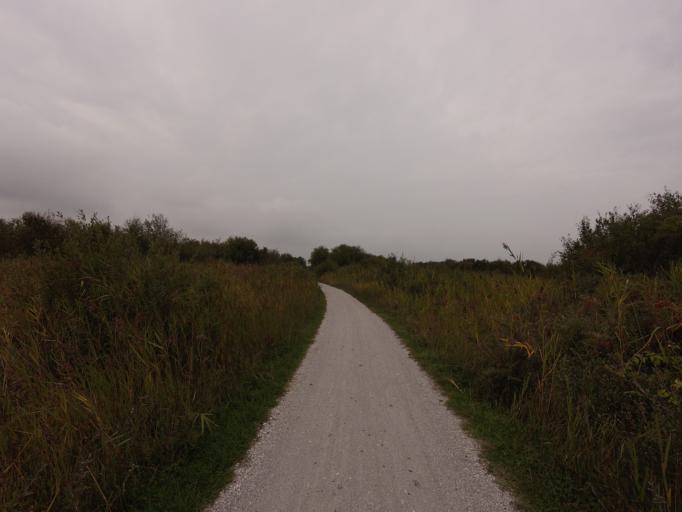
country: NL
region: Friesland
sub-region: Gemeente Schiermonnikoog
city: Schiermonnikoog
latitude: 53.4901
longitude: 6.2015
